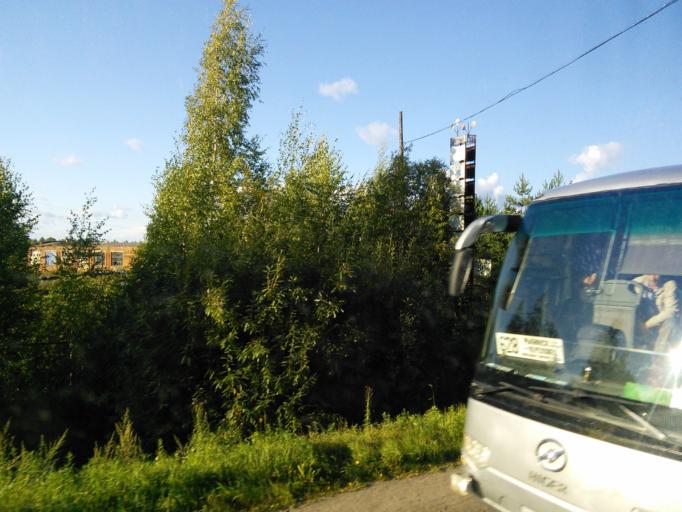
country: RU
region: Jaroslavl
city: Poshekhon'ye
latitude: 58.4978
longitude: 39.1034
